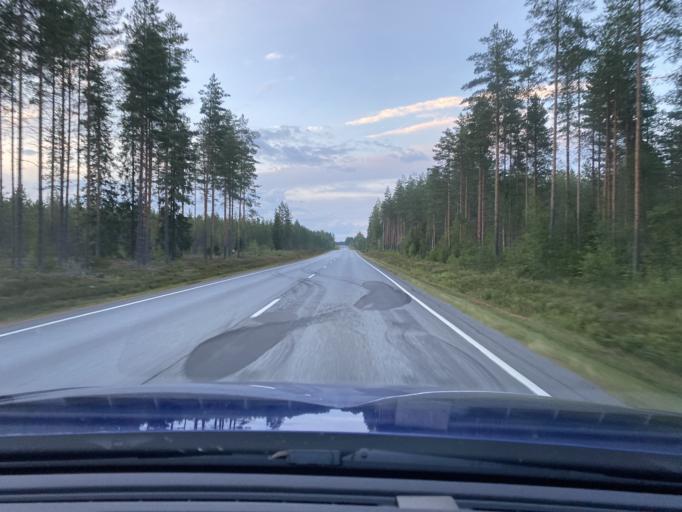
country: FI
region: Satakunta
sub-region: Pohjois-Satakunta
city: Honkajoki
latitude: 62.0266
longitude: 22.2318
